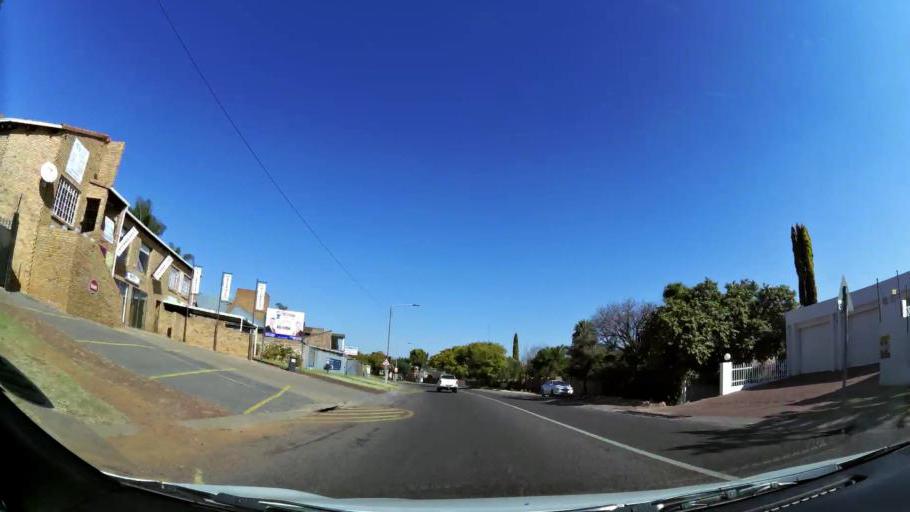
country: ZA
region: Gauteng
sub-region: City of Tshwane Metropolitan Municipality
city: Centurion
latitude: -25.8125
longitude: 28.2689
